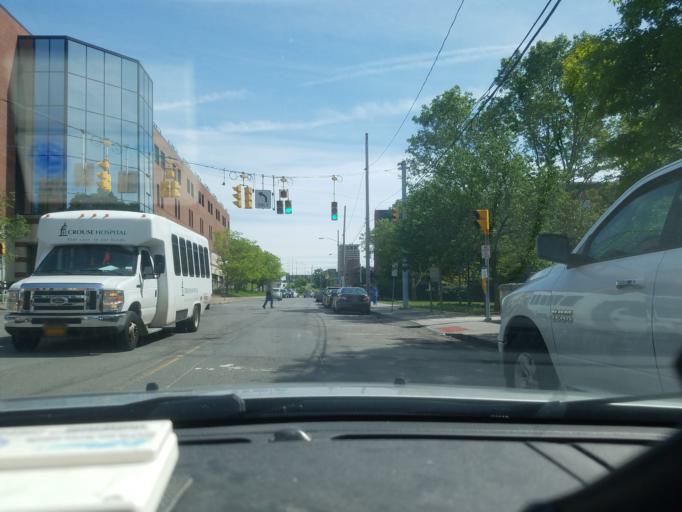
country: US
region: New York
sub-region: Onondaga County
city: Syracuse
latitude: 43.0409
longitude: -76.1378
